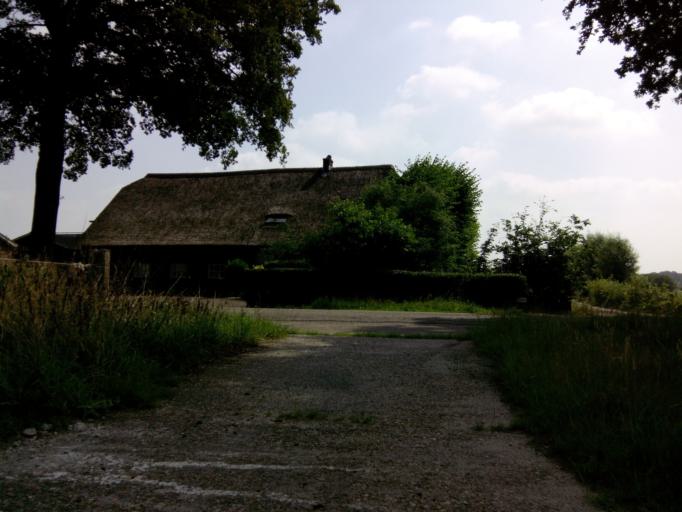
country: NL
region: Utrecht
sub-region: Gemeente Woudenberg
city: Woudenberg
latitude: 52.0957
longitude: 5.3881
